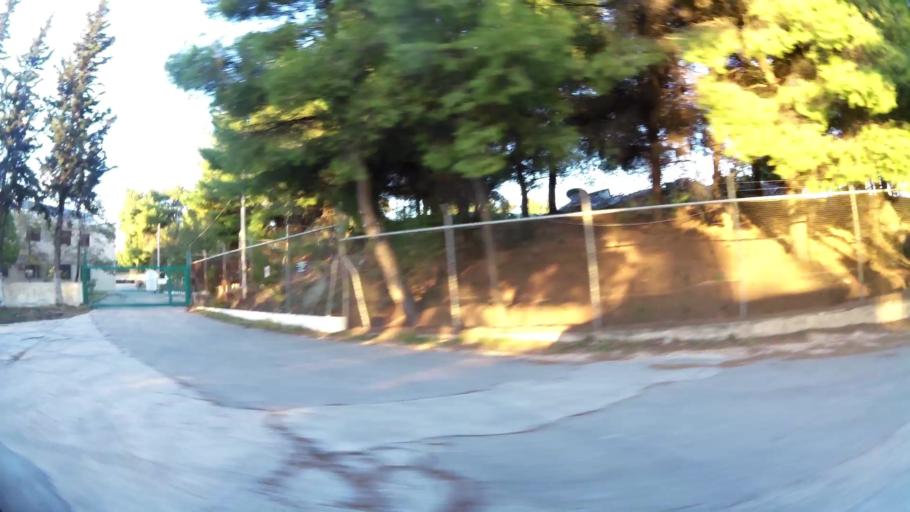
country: GR
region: Attica
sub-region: Nomarchia Anatolikis Attikis
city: Kryoneri
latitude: 38.1305
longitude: 23.8338
